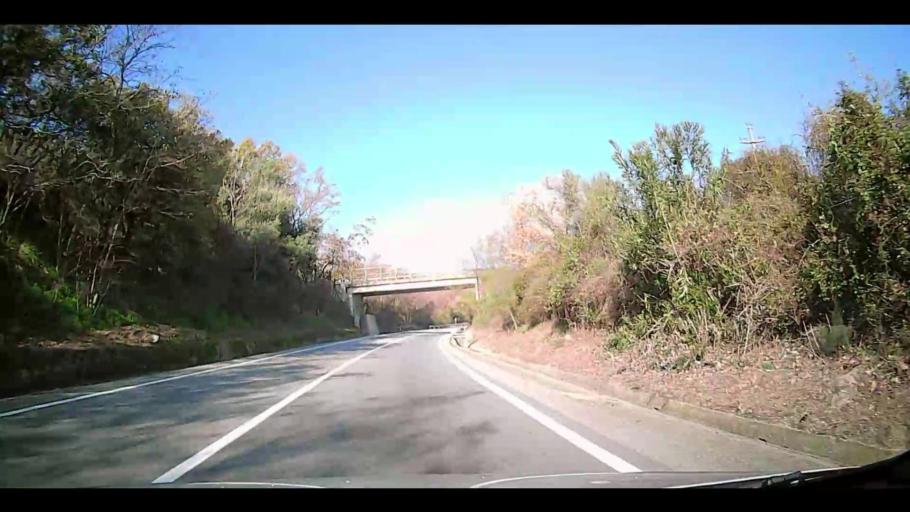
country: IT
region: Calabria
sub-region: Provincia di Crotone
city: Caccuri
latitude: 39.2037
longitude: 16.8075
